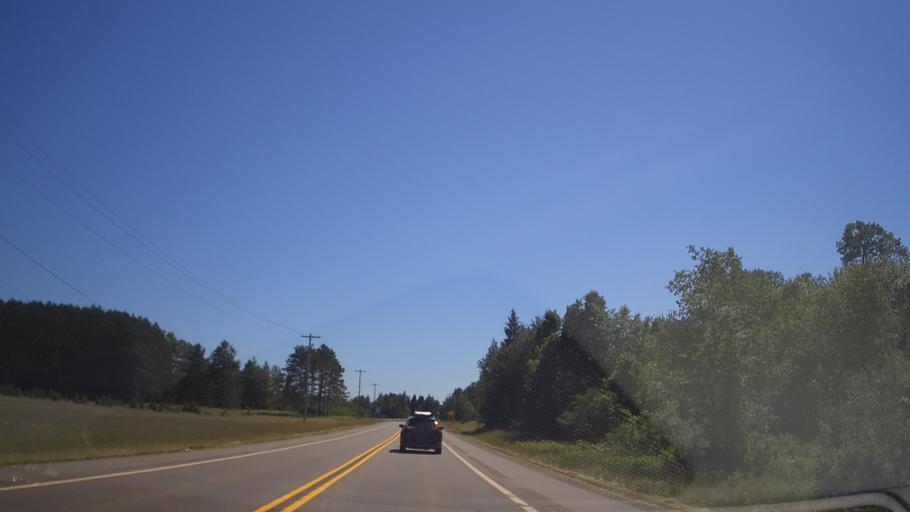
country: US
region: Michigan
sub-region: Mackinac County
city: Saint Ignace
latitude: 45.6138
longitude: -84.7809
